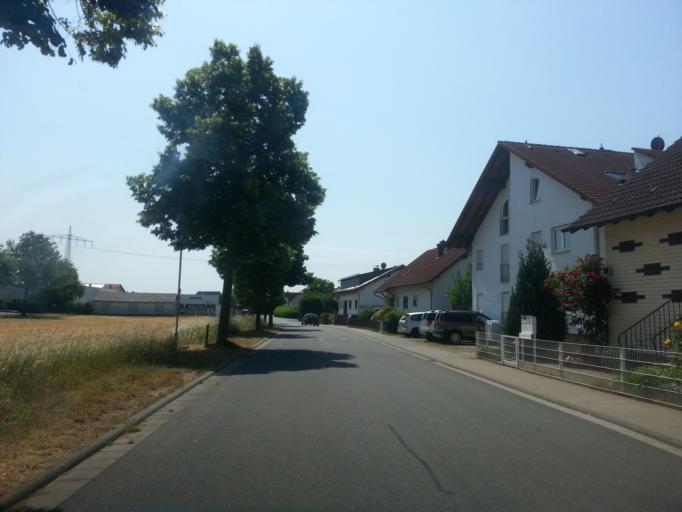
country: DE
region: Hesse
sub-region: Regierungsbezirk Darmstadt
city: Munster
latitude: 49.9310
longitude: 8.8653
